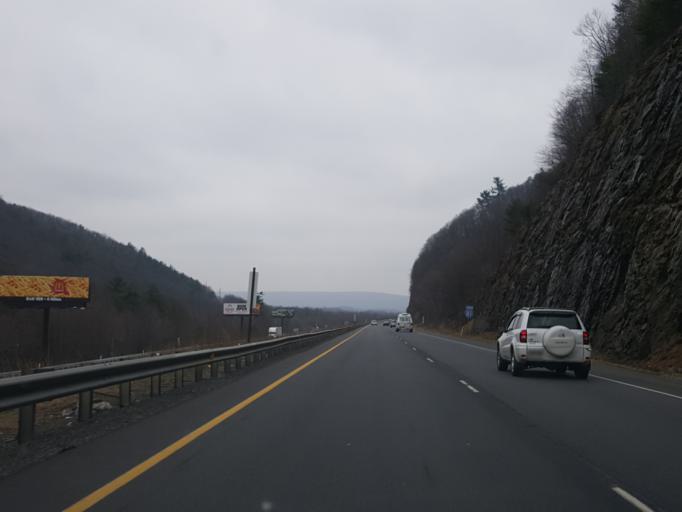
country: US
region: Pennsylvania
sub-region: Schuylkill County
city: Pine Grove
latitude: 40.5861
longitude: -76.4107
